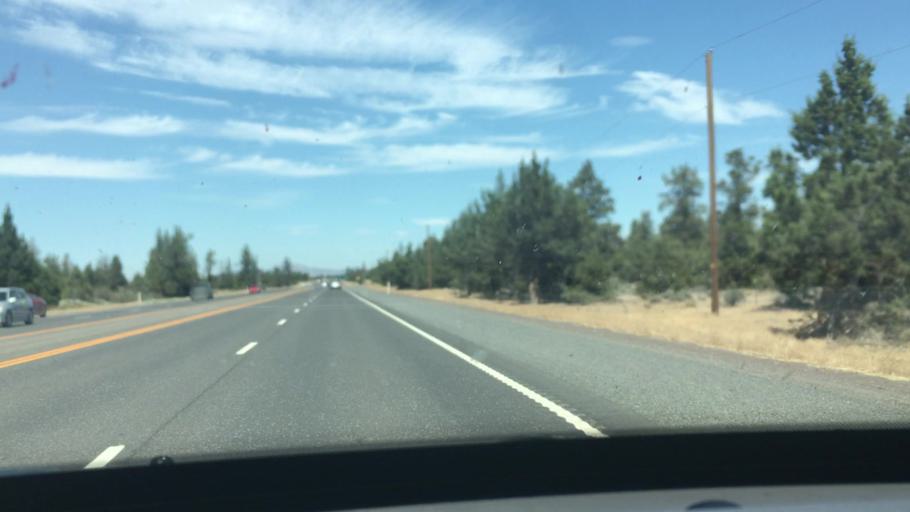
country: US
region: Oregon
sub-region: Deschutes County
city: Bend
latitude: 44.1675
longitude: -121.2539
